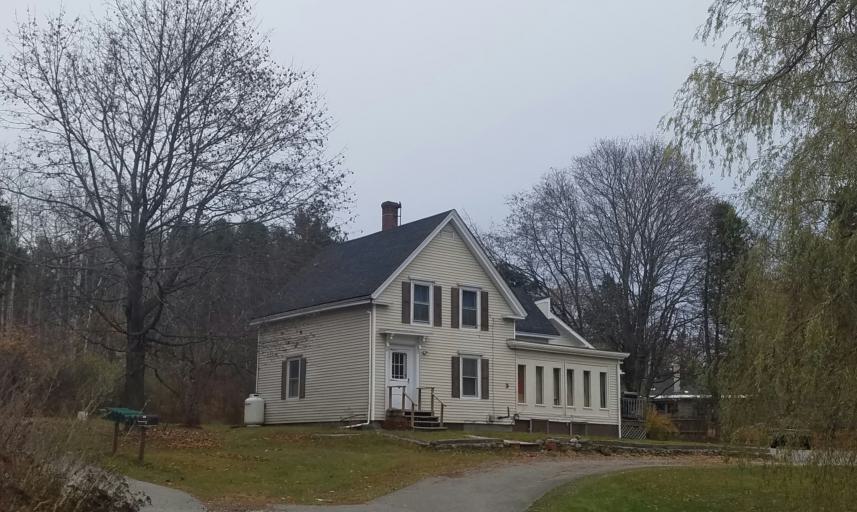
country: US
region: Maine
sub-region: Waldo County
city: Belfast
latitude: 44.4293
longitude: -68.9850
